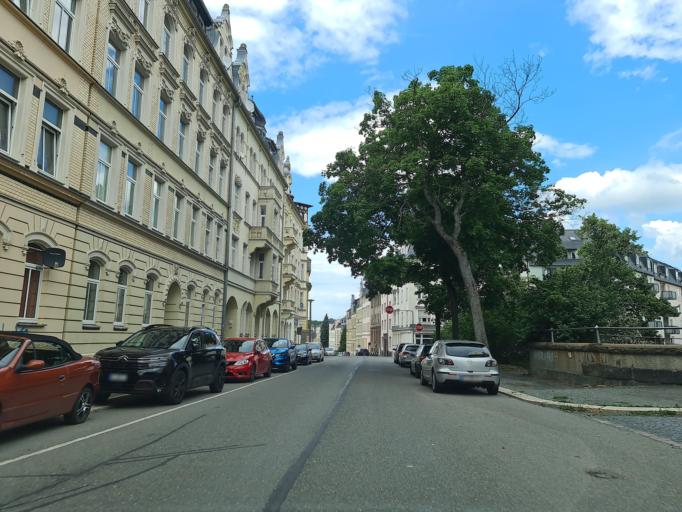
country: DE
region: Saxony
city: Plauen
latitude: 50.5139
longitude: 12.1282
